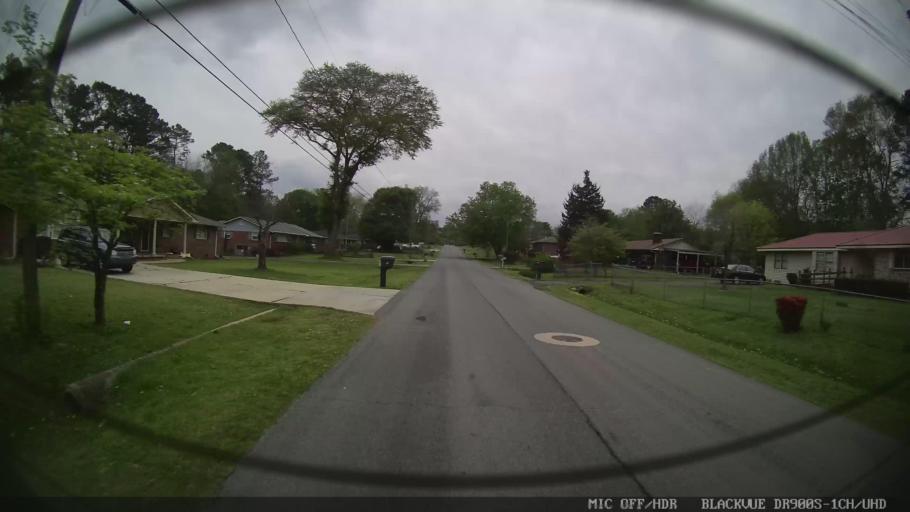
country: US
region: Georgia
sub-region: Bartow County
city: Cartersville
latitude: 34.1996
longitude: -84.8168
